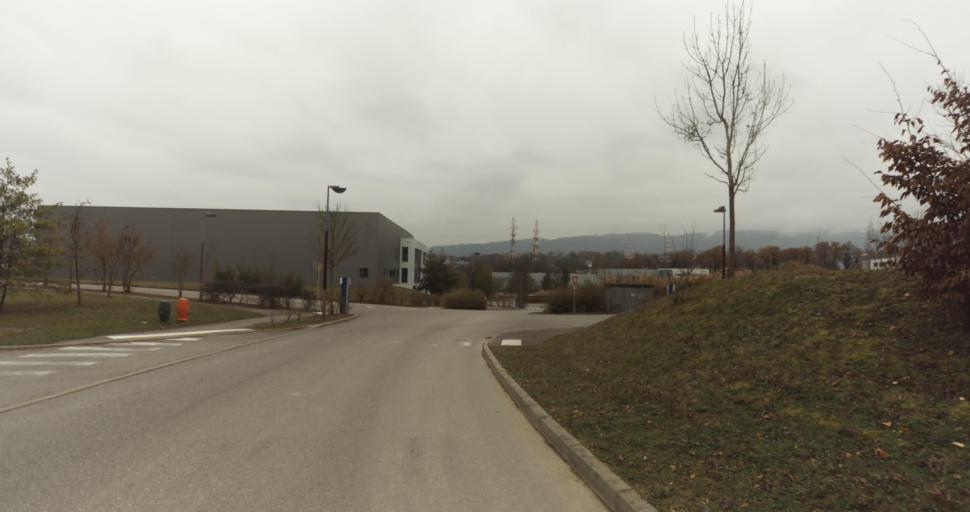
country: FR
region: Rhone-Alpes
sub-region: Departement de la Haute-Savoie
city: Seynod
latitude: 45.8930
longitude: 6.0767
